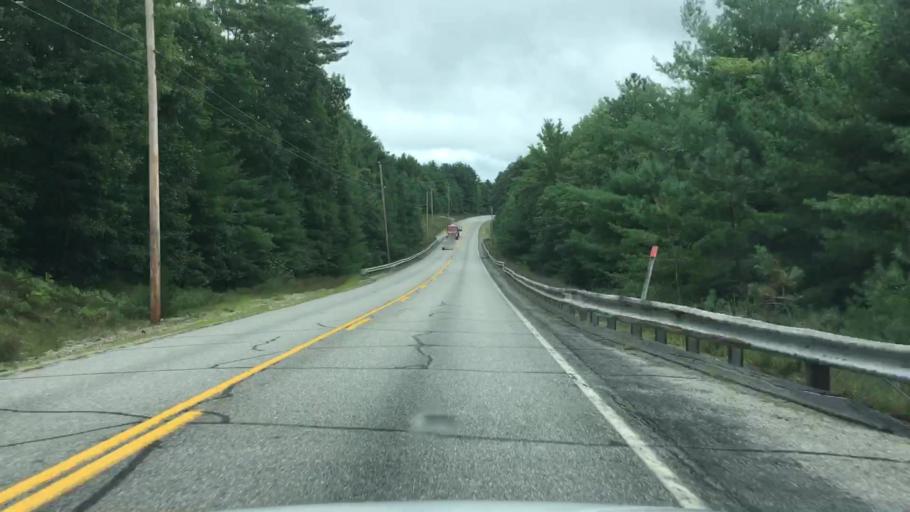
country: US
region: Maine
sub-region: Oxford County
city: Hiram
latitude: 43.8982
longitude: -70.8321
